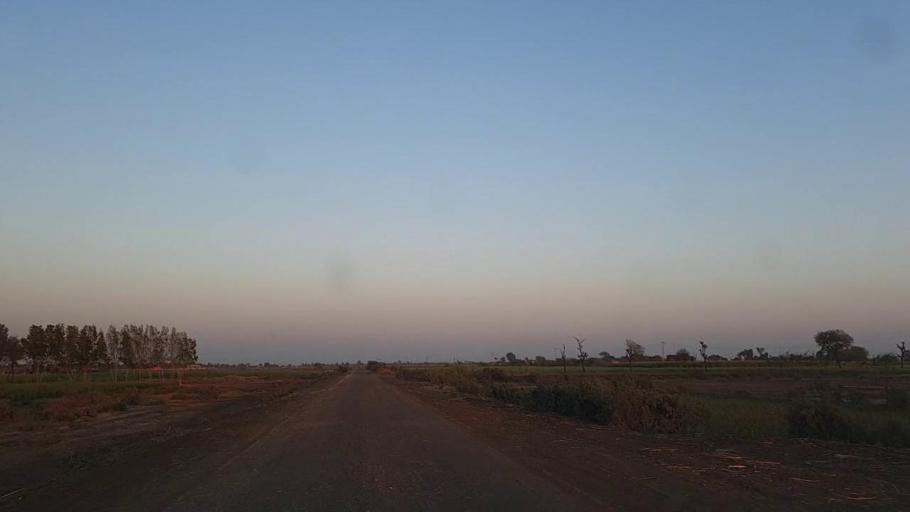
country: PK
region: Sindh
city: Samaro
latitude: 25.3093
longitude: 69.3811
